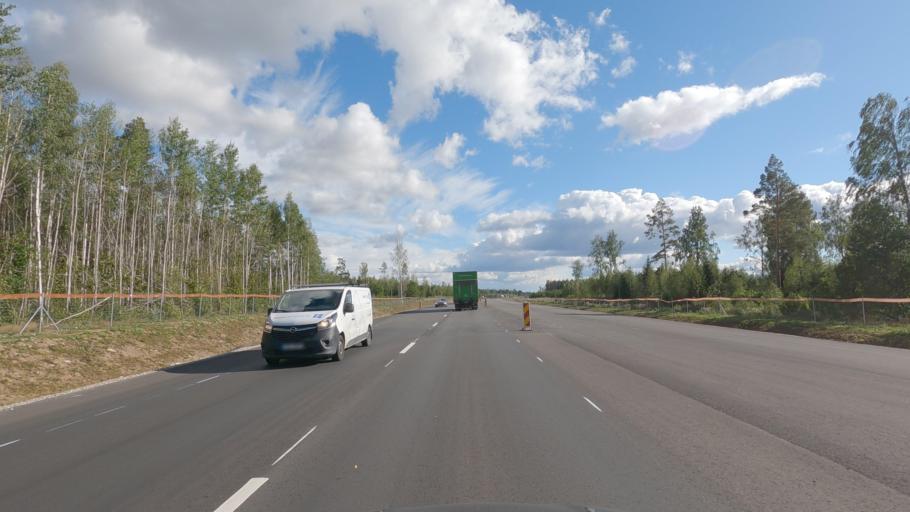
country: EE
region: Jaervamaa
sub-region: Paide linn
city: Paide
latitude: 58.9831
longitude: 25.6000
